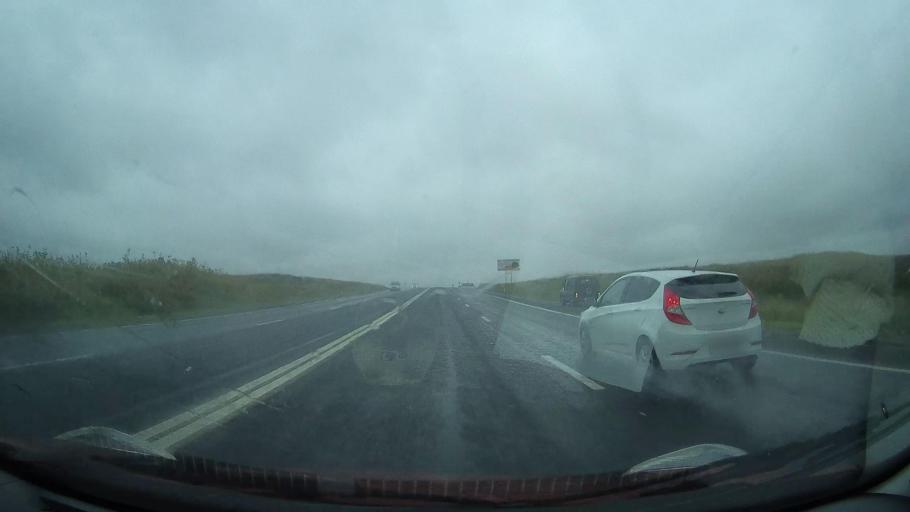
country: RU
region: Stavropol'skiy
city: Nevinnomyssk
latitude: 44.6239
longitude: 42.0683
